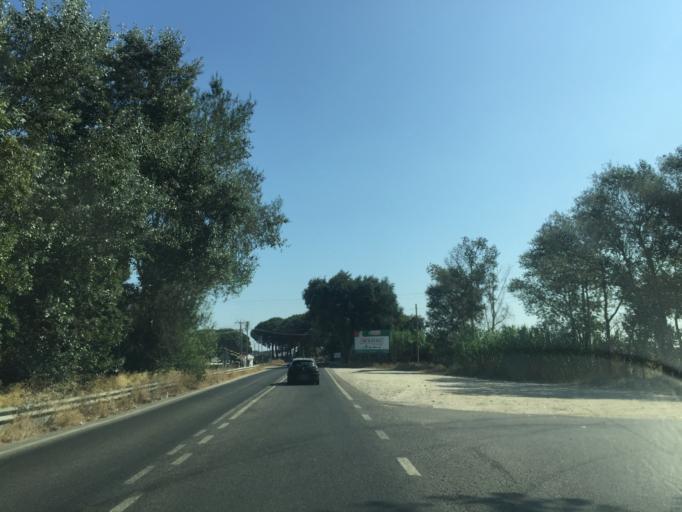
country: PT
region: Santarem
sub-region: Almeirim
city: Almeirim
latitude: 39.2199
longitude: -8.6145
